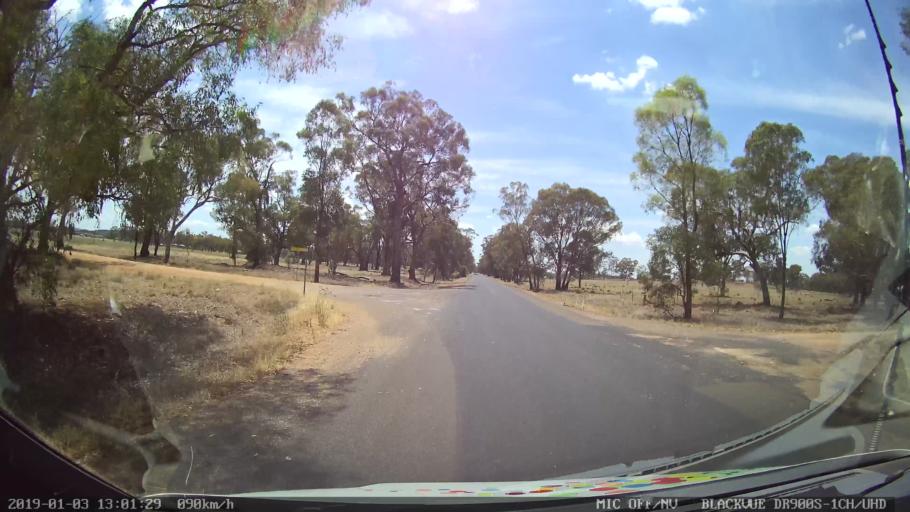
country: AU
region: New South Wales
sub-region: Cabonne
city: Canowindra
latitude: -33.6240
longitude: 148.4187
